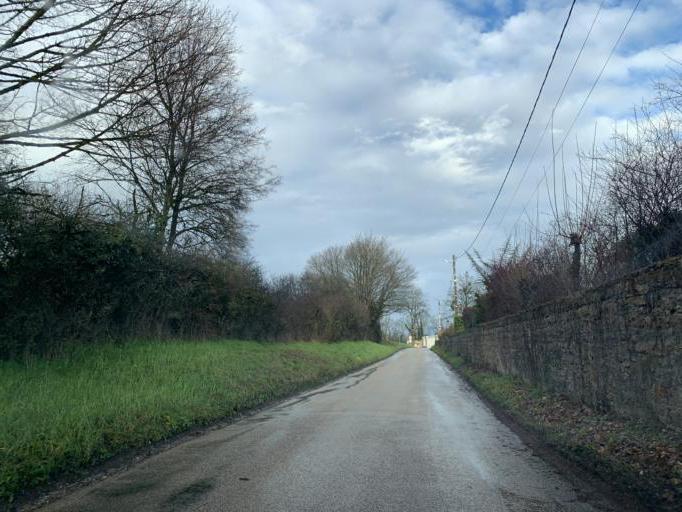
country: FR
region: Rhone-Alpes
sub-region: Departement du Rhone
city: Rillieux-la-Pape
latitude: 45.8185
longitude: 4.9209
